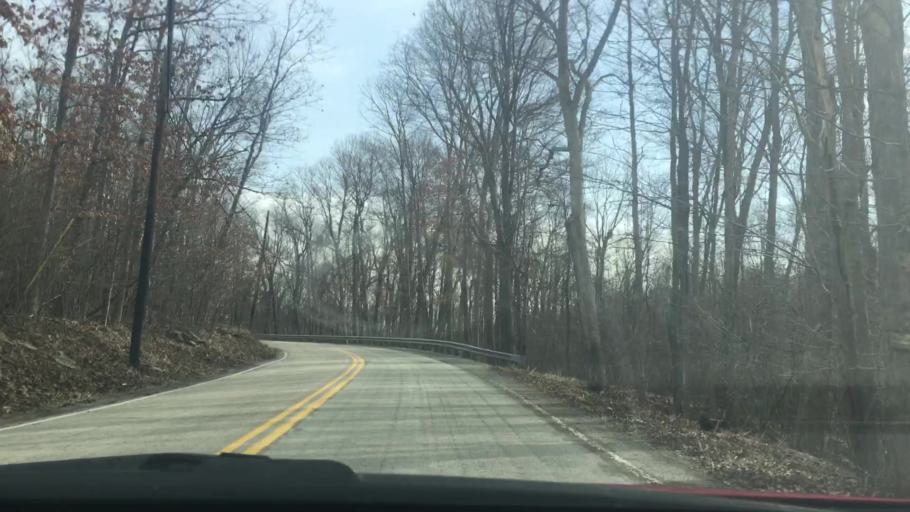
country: US
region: Pennsylvania
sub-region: Fayette County
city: Hopwood
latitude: 39.8241
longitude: -79.5439
